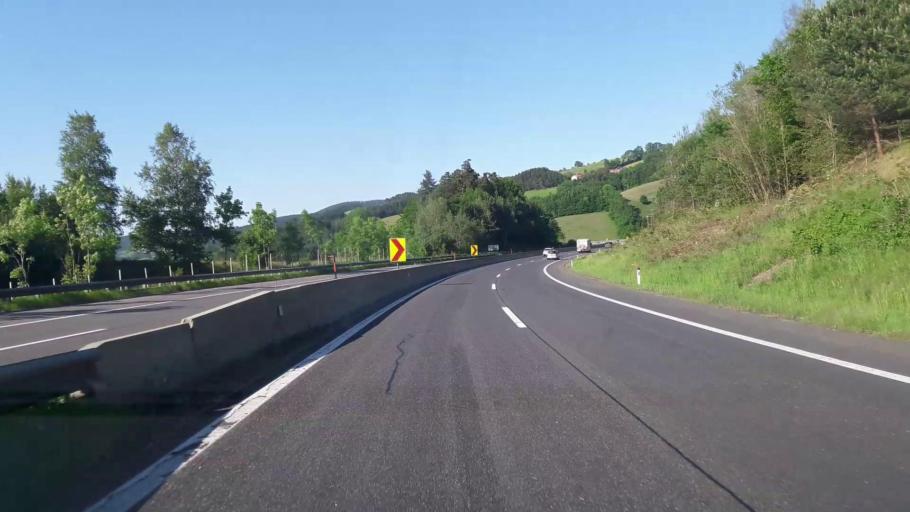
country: AT
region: Lower Austria
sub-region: Politischer Bezirk Neunkirchen
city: Grimmenstein
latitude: 47.6010
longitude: 16.1253
